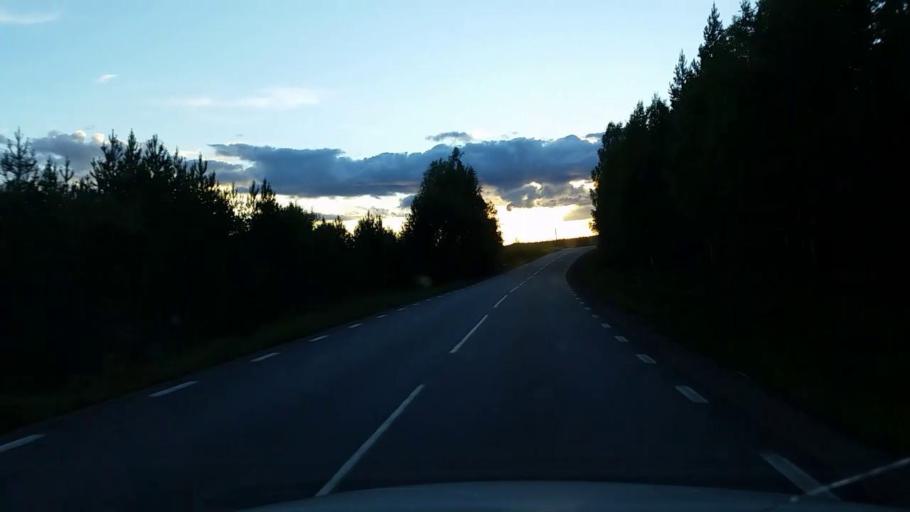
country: SE
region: Gaevleborg
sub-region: Ljusdals Kommun
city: Farila
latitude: 62.1022
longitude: 15.7790
